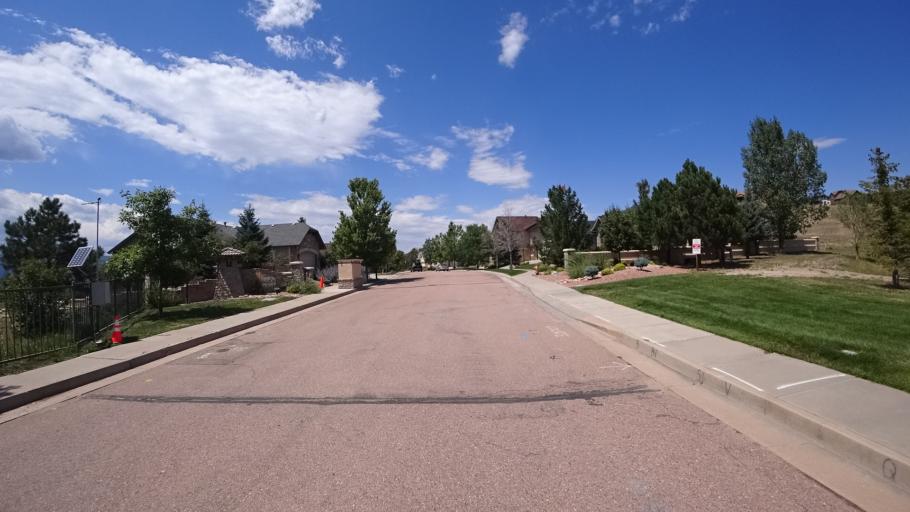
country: US
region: Colorado
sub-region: El Paso County
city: Black Forest
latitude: 38.9698
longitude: -104.7678
